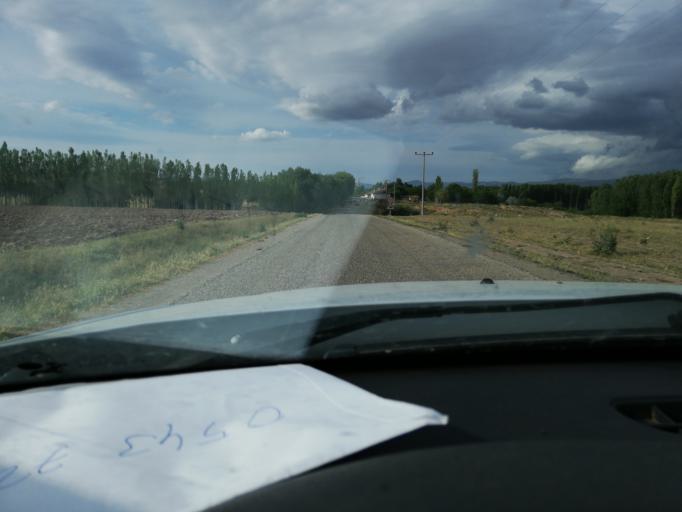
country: TR
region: Kirsehir
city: Kirsehir
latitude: 39.0211
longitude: 34.1233
